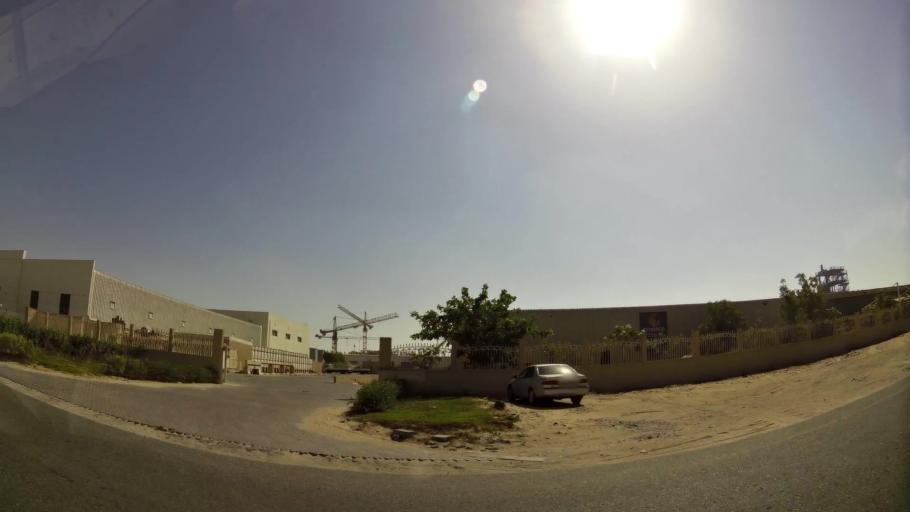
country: AE
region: Dubai
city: Dubai
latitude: 24.9330
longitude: 55.0561
